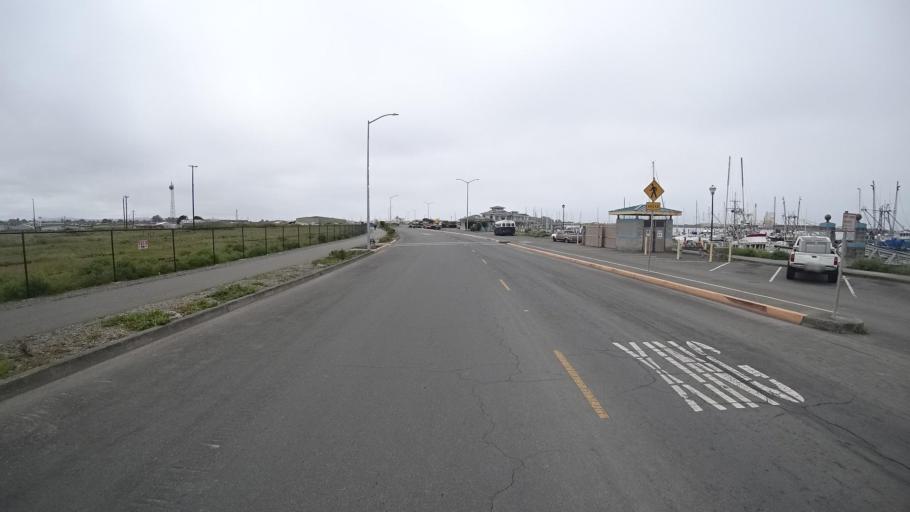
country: US
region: California
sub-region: Humboldt County
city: Eureka
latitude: 40.8033
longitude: -124.1767
